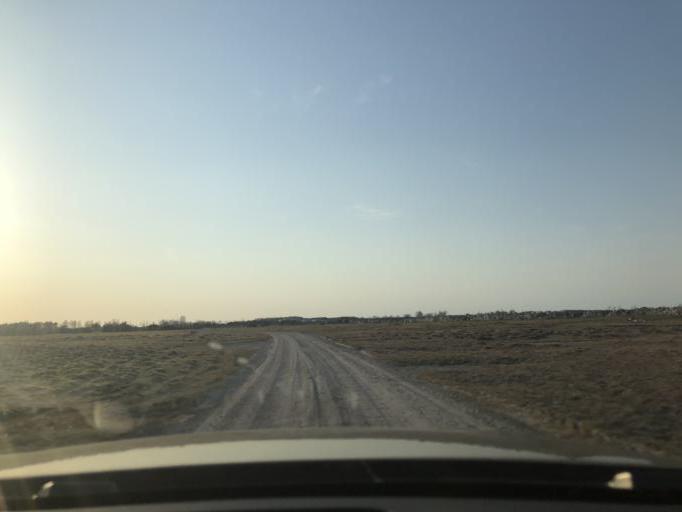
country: SE
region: Kalmar
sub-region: Morbylanga Kommun
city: Sodra Sandby
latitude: 56.5572
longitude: 16.6347
